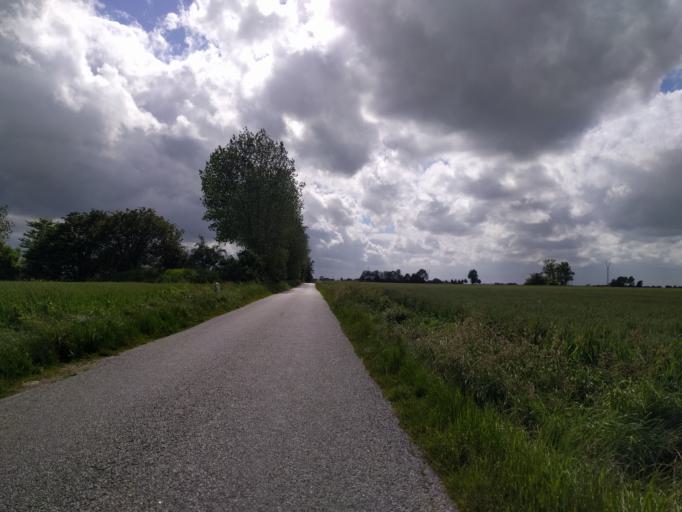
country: DK
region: South Denmark
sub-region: Kerteminde Kommune
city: Munkebo
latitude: 55.4501
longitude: 10.5174
